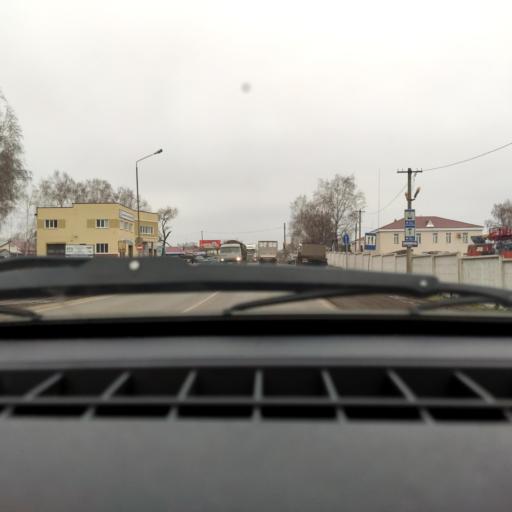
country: RU
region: Bashkortostan
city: Chishmy
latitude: 54.5849
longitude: 55.3852
